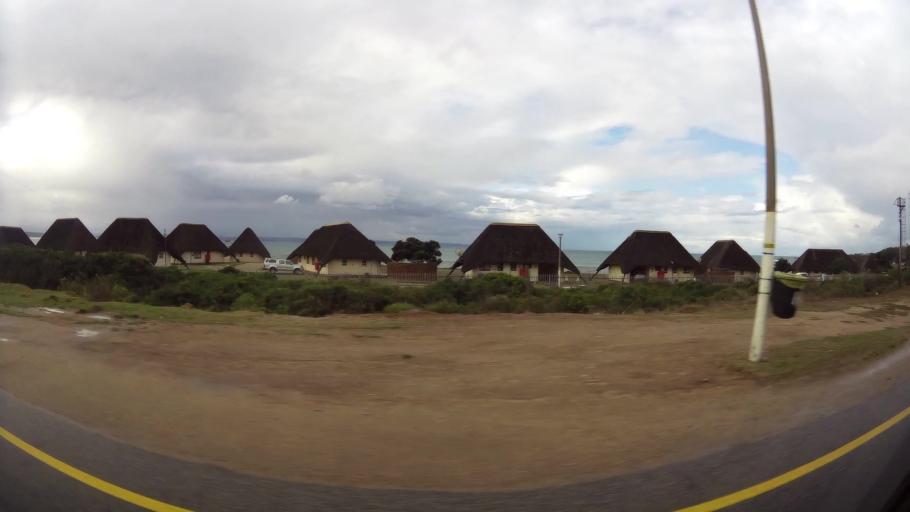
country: ZA
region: Western Cape
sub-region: Eden District Municipality
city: Mossel Bay
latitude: -34.1692
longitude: 22.1208
